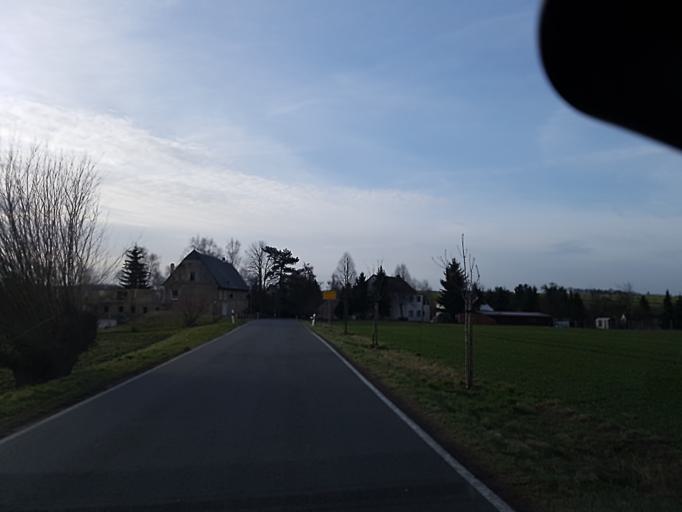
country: DE
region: Saxony
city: Bockelwitz
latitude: 51.1707
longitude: 12.9791
